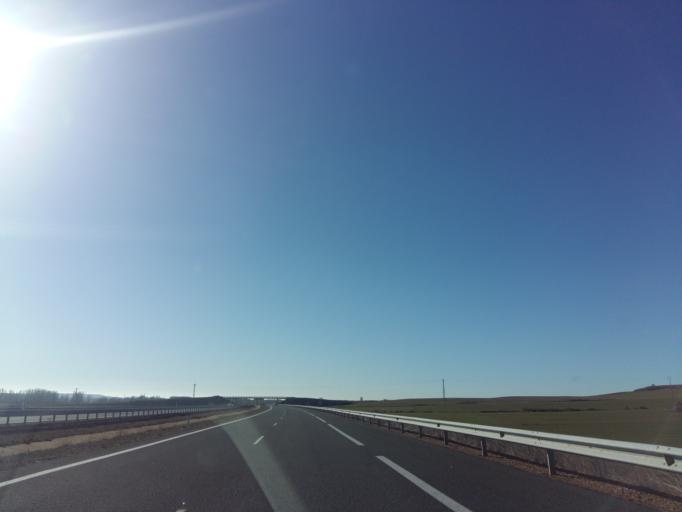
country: ES
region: Castille and Leon
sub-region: Provincia de Palencia
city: Espinosa de Villagonzalo
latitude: 42.4782
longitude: -4.3863
